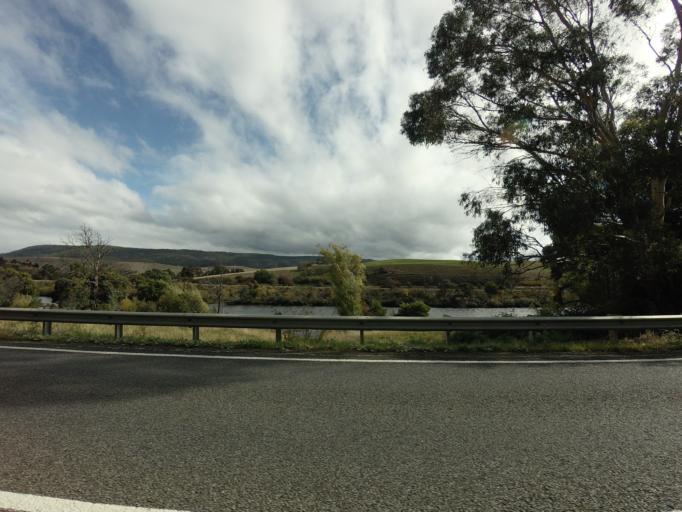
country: AU
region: Tasmania
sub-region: Derwent Valley
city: New Norfolk
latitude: -42.7285
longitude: 146.9563
